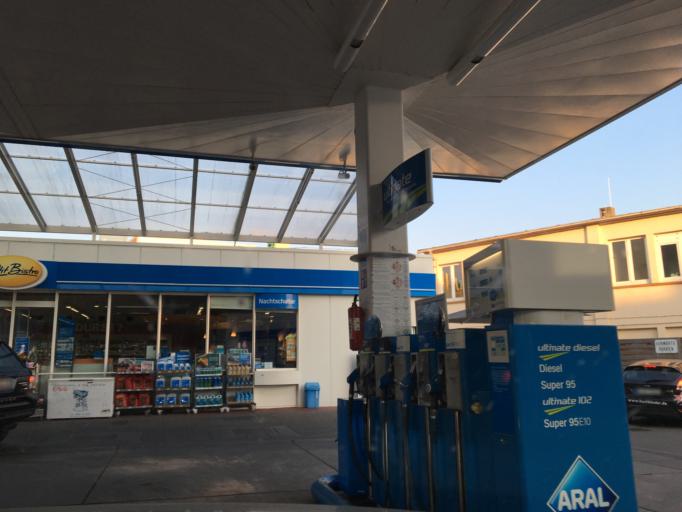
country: DE
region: Hesse
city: Niederrad
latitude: 50.1290
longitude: 8.6242
